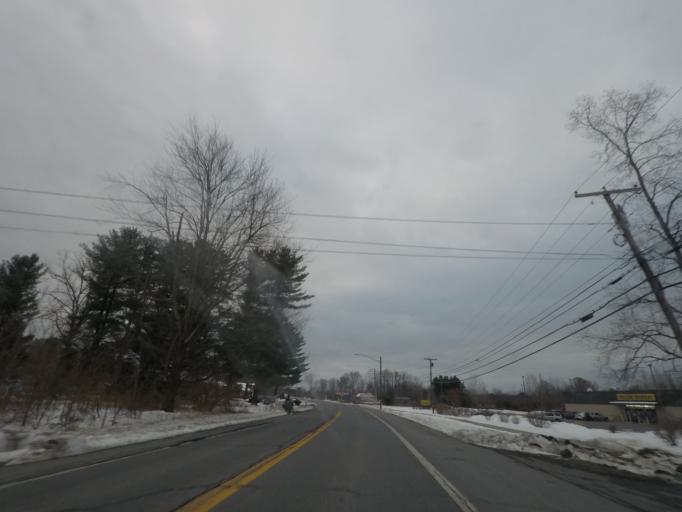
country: US
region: New York
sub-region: Ulster County
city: Plattekill
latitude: 41.6600
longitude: -74.1121
